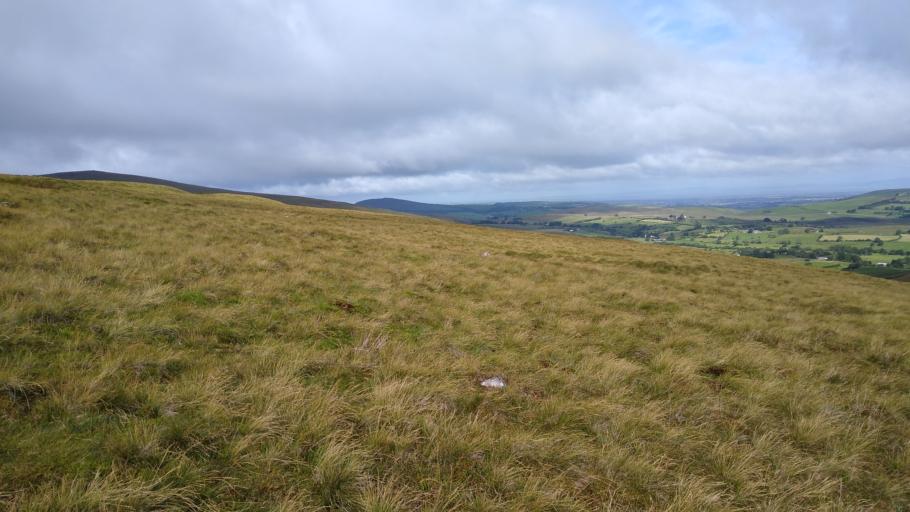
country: GB
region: England
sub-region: Cumbria
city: Keswick
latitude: 54.7177
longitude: -3.0678
